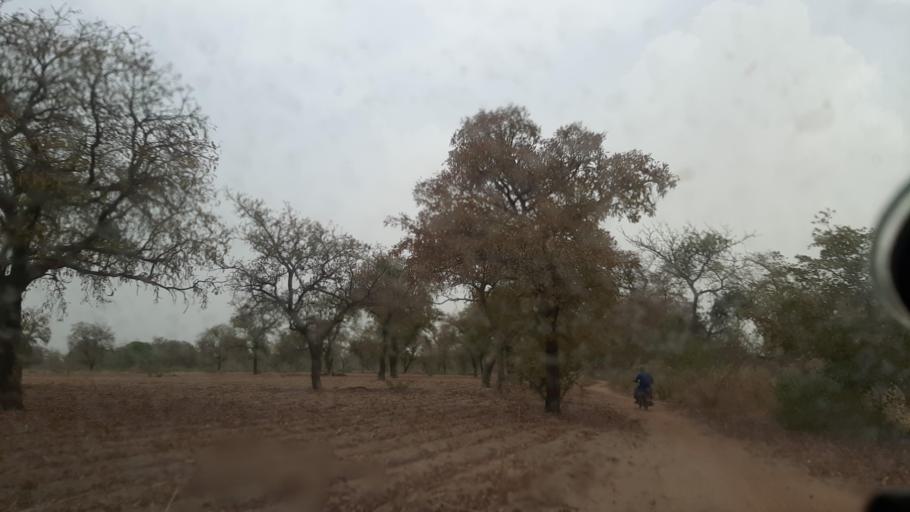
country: BF
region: Boucle du Mouhoun
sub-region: Province des Banwa
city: Salanso
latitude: 11.8568
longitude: -4.4311
